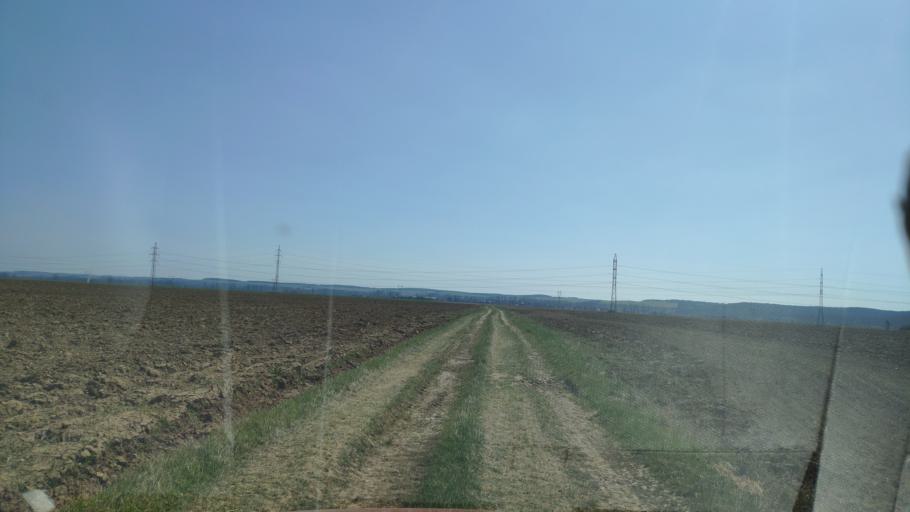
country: SK
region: Kosicky
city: Moldava nad Bodvou
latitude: 48.6016
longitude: 20.9445
